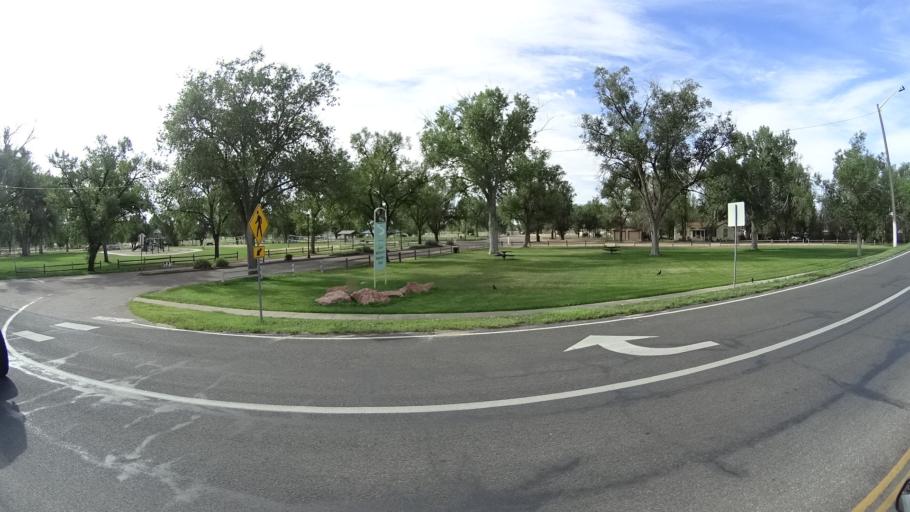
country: US
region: Colorado
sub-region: El Paso County
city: Fountain
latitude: 38.6839
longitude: -104.6933
